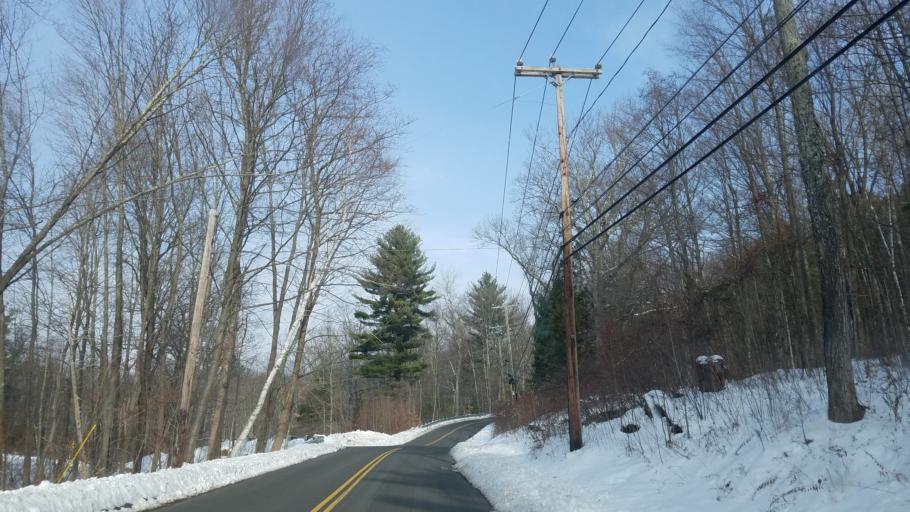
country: US
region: Connecticut
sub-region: Hartford County
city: Canton Valley
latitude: 41.8457
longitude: -72.9004
